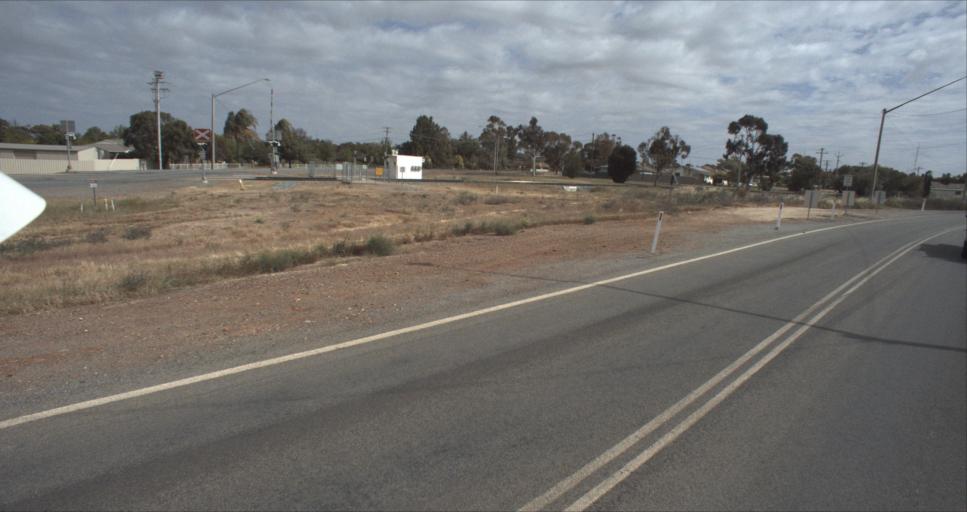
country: AU
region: New South Wales
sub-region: Leeton
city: Leeton
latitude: -34.5692
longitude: 146.3947
